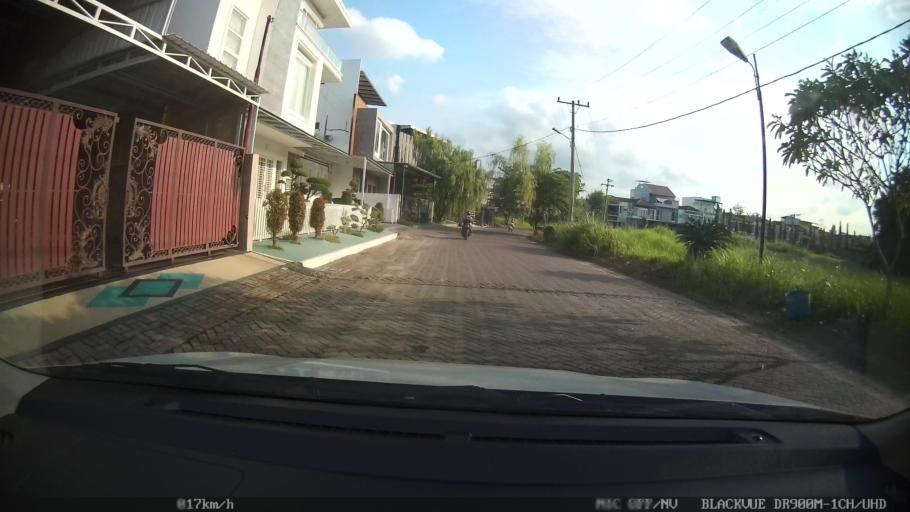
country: ID
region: North Sumatra
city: Medan
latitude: 3.6210
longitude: 98.6477
